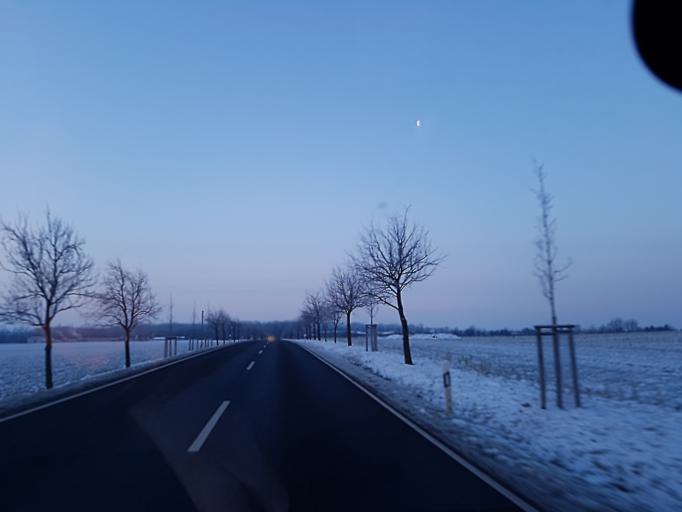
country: DE
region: Saxony
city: Strehla
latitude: 51.3225
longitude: 13.1976
